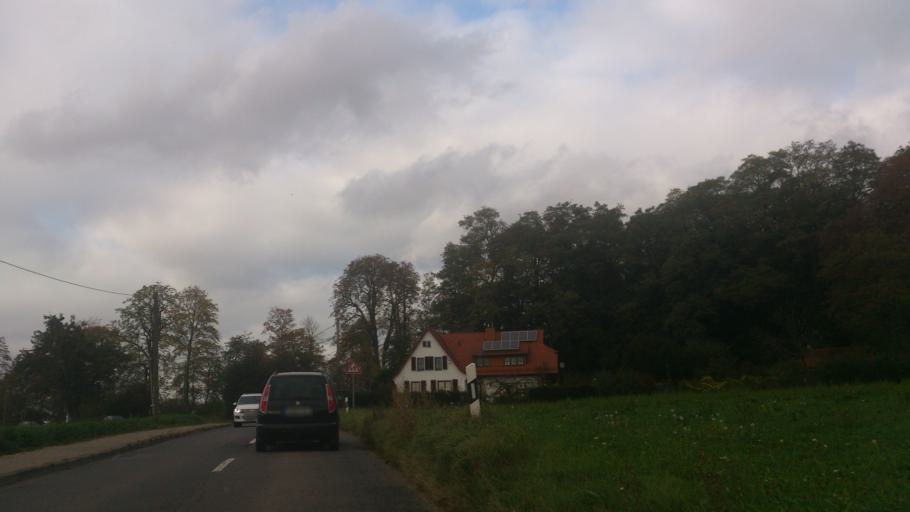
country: DE
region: Baden-Wuerttemberg
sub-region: Karlsruhe Region
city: Heidelberg
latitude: 49.3885
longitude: 8.7045
